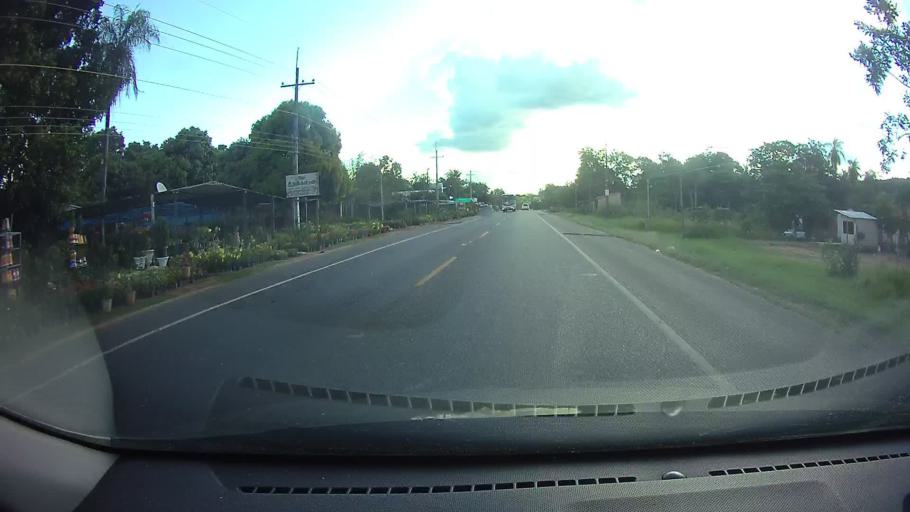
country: PY
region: Cordillera
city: Eusebio Ayala
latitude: -25.3786
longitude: -57.0351
